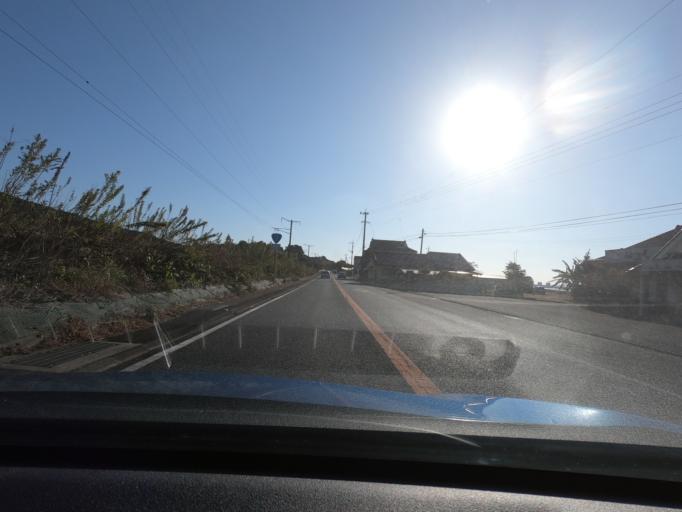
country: JP
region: Kagoshima
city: Izumi
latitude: 32.1398
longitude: 130.3543
